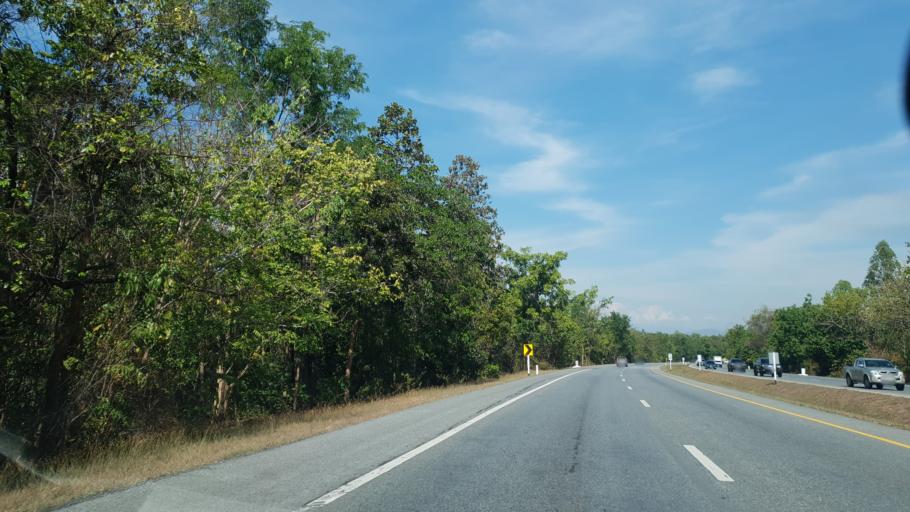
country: TH
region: Uttaradit
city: Thong Saen Khan
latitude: 17.4251
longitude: 100.2257
